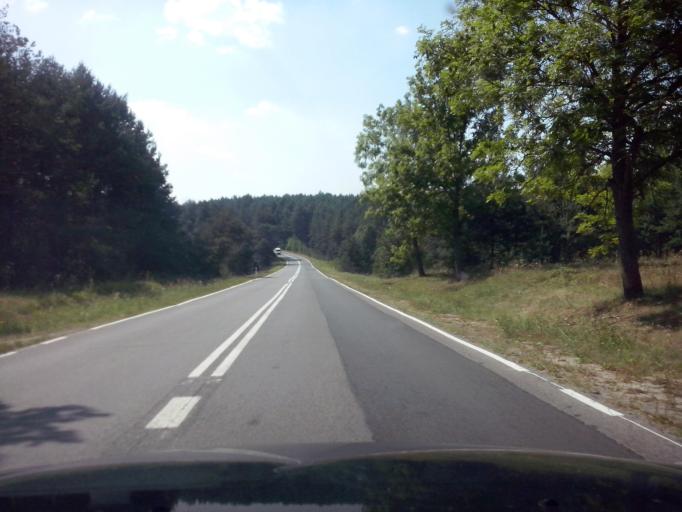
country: PL
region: Swietokrzyskie
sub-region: Powiat kielecki
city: Rakow
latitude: 50.6665
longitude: 21.0319
